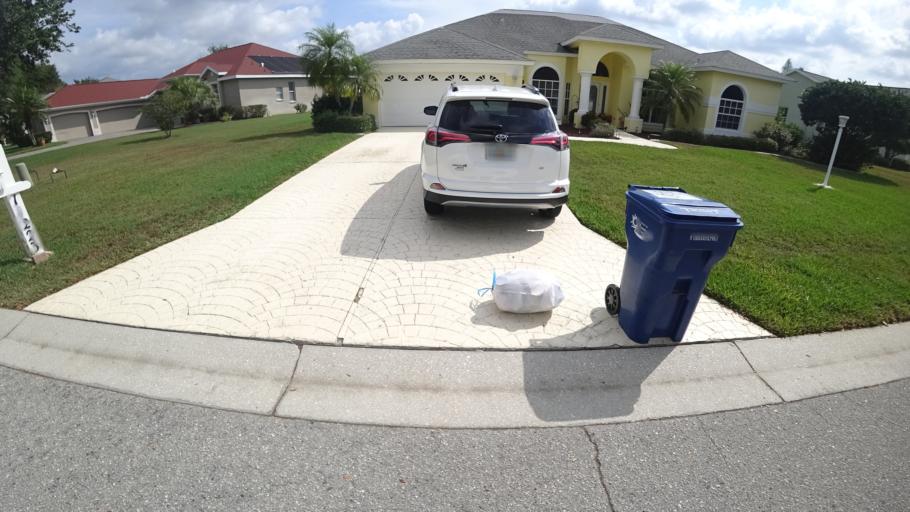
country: US
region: Florida
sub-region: Manatee County
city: Ellenton
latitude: 27.5364
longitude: -82.4493
